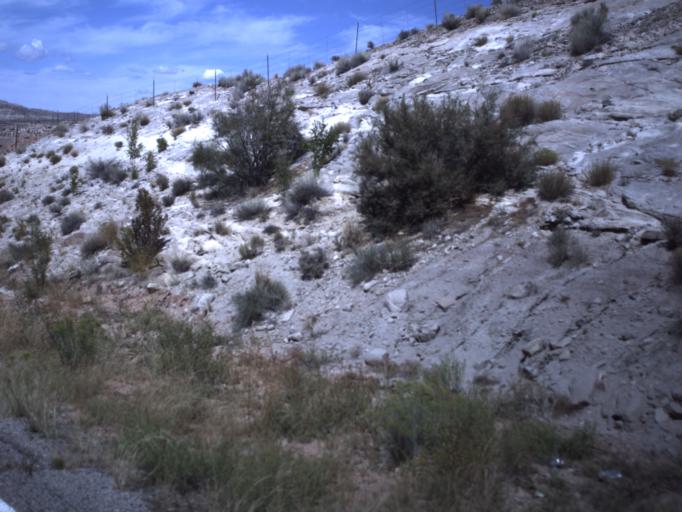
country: US
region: Utah
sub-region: San Juan County
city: Blanding
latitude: 37.2810
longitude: -109.3780
